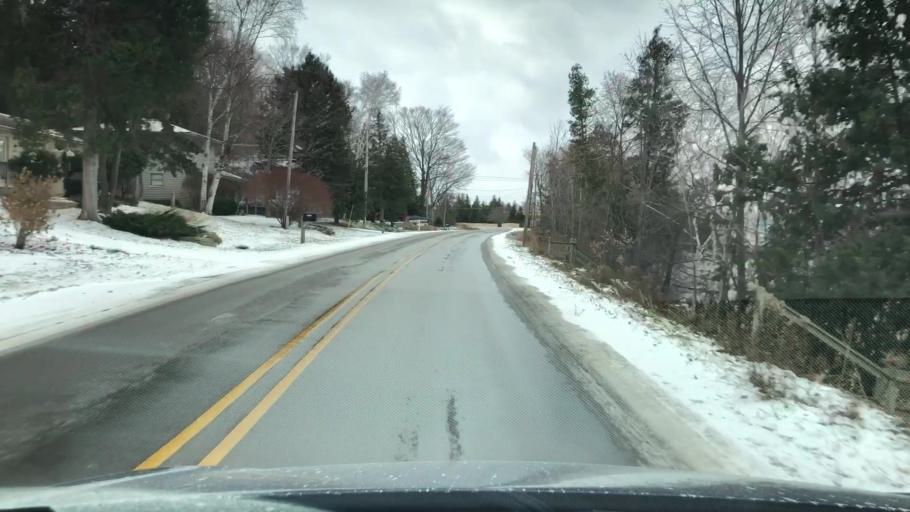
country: US
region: Michigan
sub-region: Leelanau County
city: Greilickville
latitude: 44.8398
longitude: -85.5601
